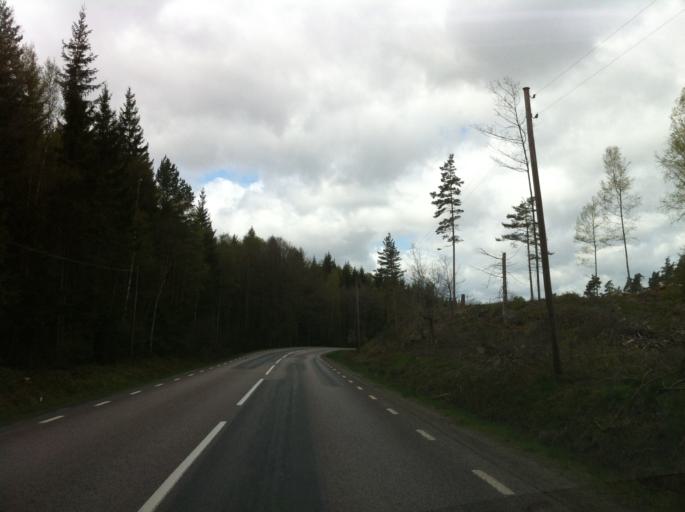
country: SE
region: Vaestra Goetaland
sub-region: Alingsas Kommun
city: Ingared
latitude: 57.8437
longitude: 12.5130
